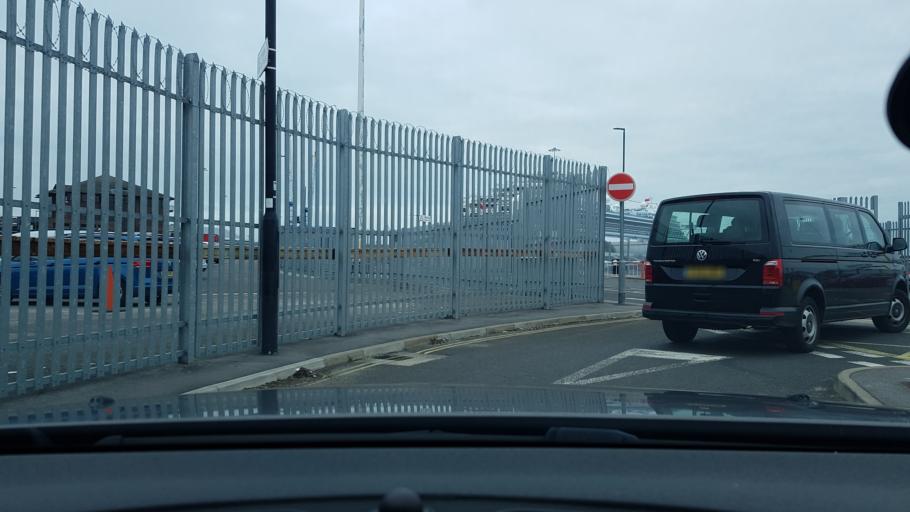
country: GB
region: England
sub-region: Southampton
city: Southampton
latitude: 50.8961
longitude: -1.4011
